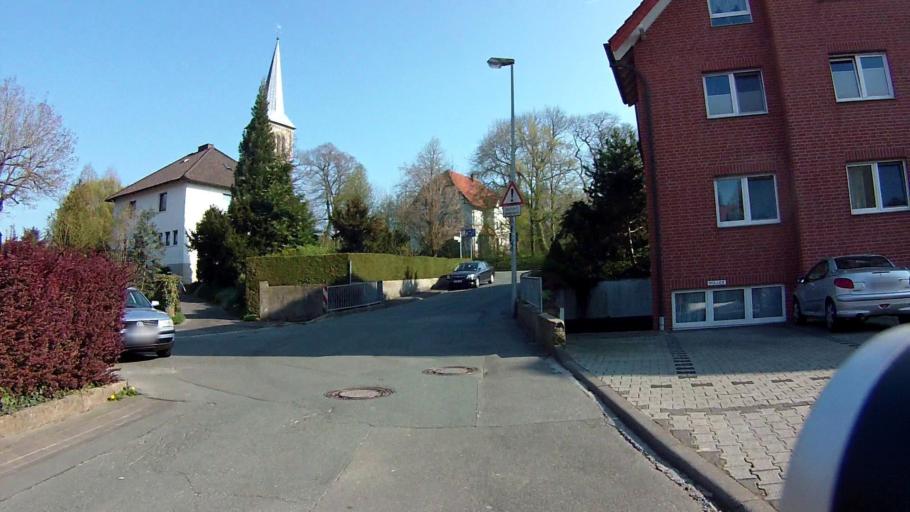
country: DE
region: North Rhine-Westphalia
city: Lichtenau
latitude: 51.6960
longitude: 8.8504
